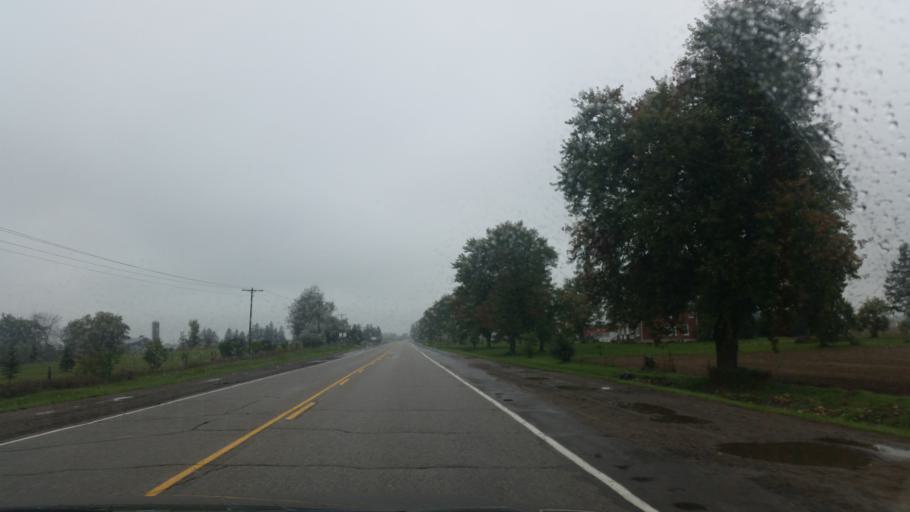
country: CA
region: Ontario
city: Waterloo
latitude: 43.5953
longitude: -80.5109
